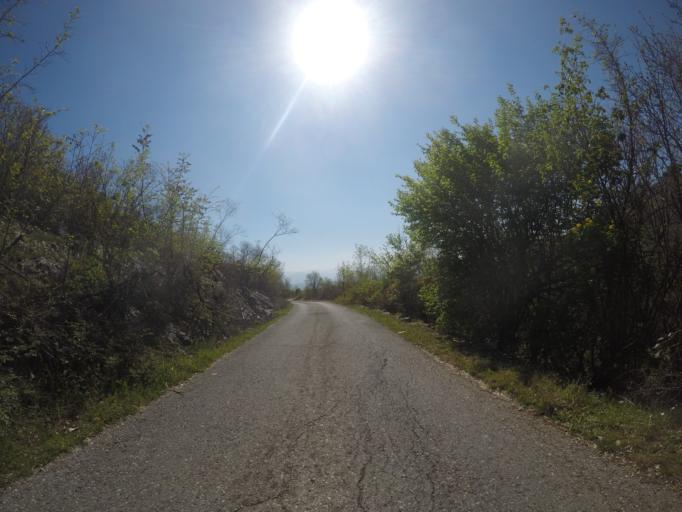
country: ME
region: Danilovgrad
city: Danilovgrad
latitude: 42.5166
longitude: 19.0629
